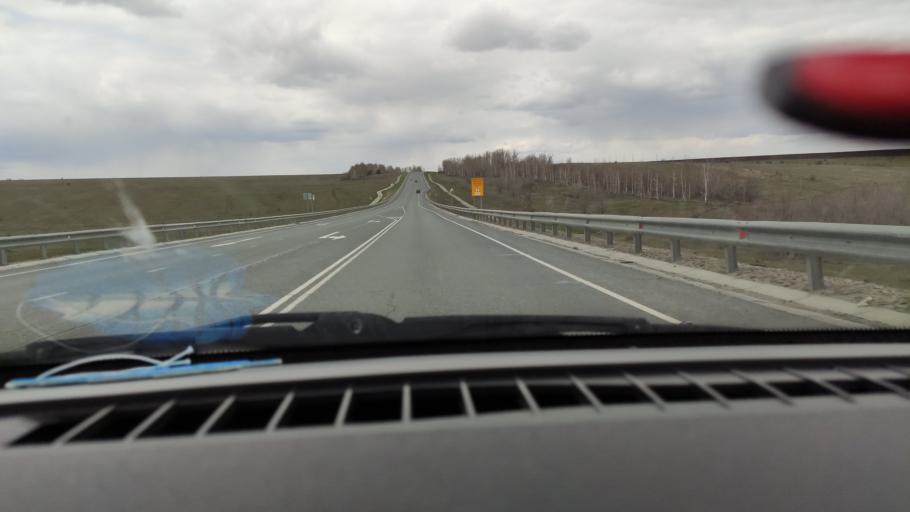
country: RU
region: Saratov
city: Shikhany
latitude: 52.1199
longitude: 47.2659
